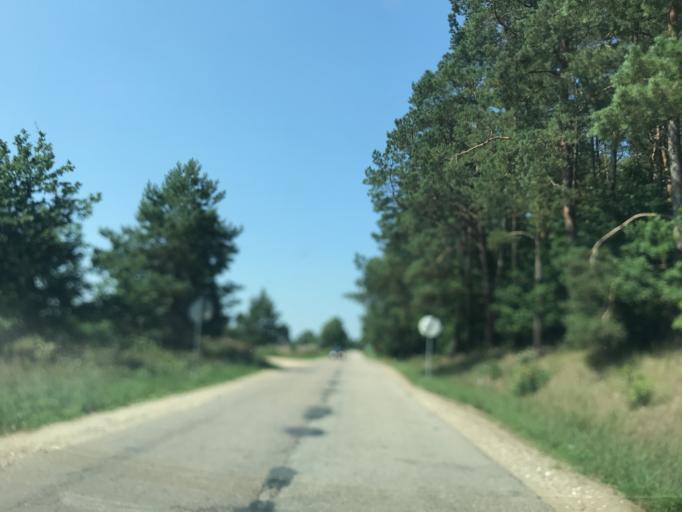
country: PL
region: Kujawsko-Pomorskie
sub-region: Powiat lipnowski
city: Chrostkowo
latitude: 52.9880
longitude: 19.2974
